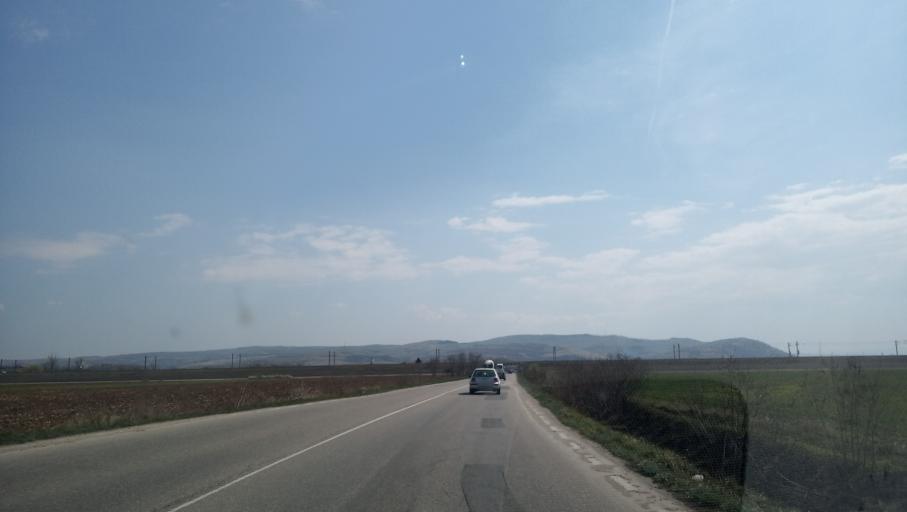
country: RO
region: Alba
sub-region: Municipiul Sebes
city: Lancram
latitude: 46.0236
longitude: 23.5360
